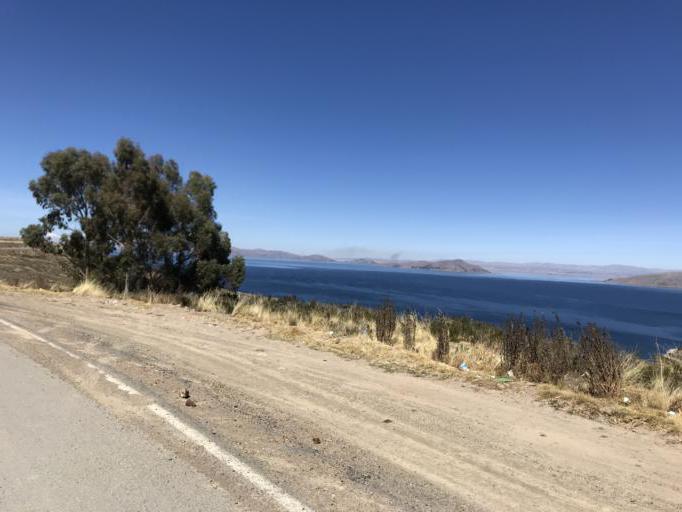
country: BO
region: La Paz
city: San Pablo
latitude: -16.1980
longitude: -68.8261
